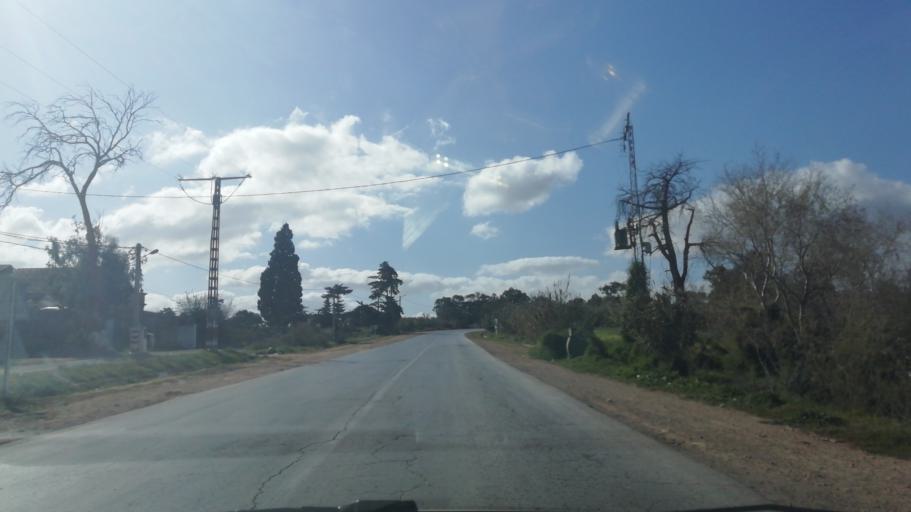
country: DZ
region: Relizane
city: Mazouna
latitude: 36.2985
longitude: 0.6579
